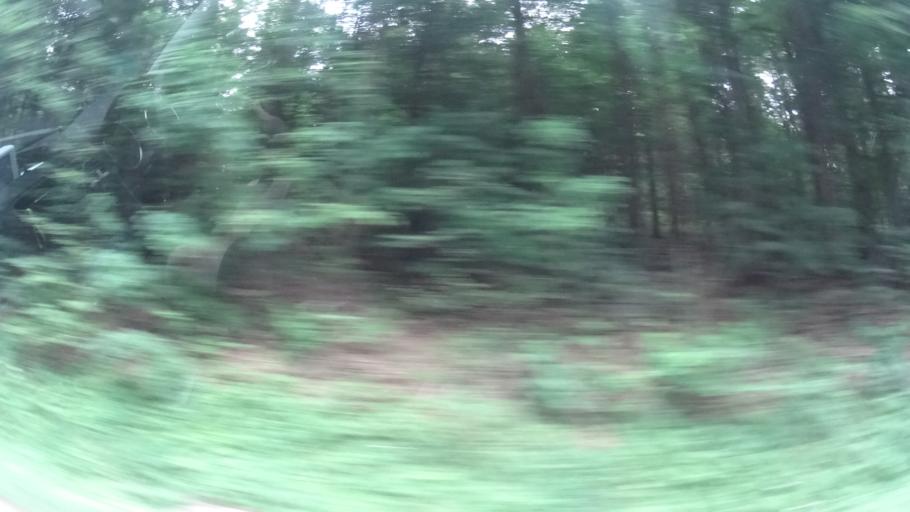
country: DE
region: North Rhine-Westphalia
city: Brakel
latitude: 51.6681
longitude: 9.1590
